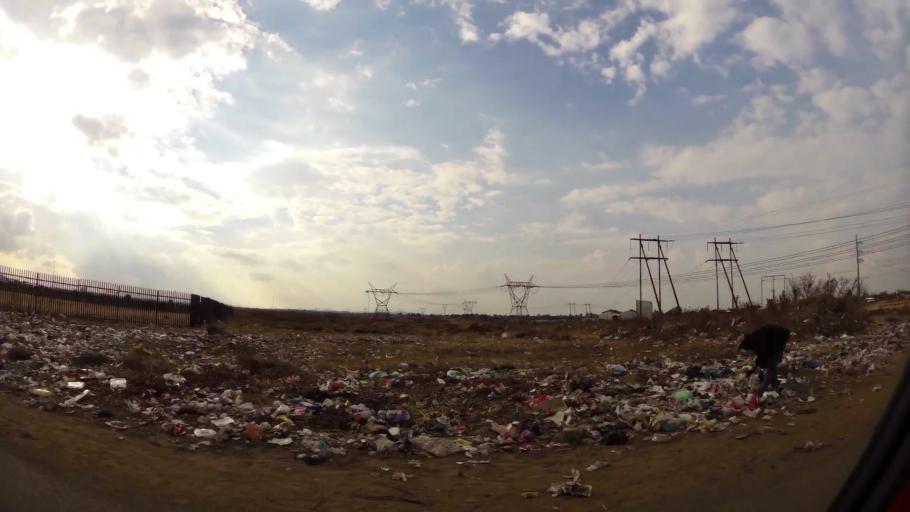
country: ZA
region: Gauteng
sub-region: Sedibeng District Municipality
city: Vereeniging
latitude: -26.6727
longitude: 27.8772
